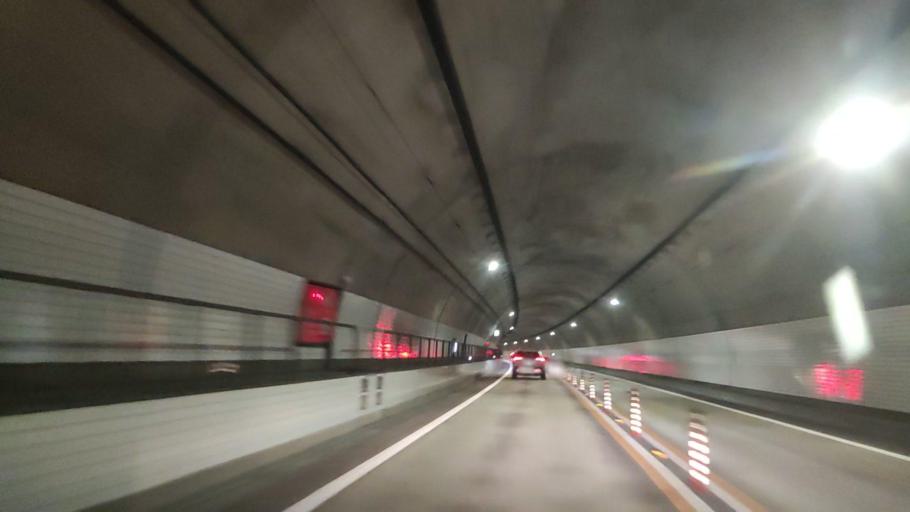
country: JP
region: Kyoto
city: Miyazu
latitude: 35.5597
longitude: 135.1232
